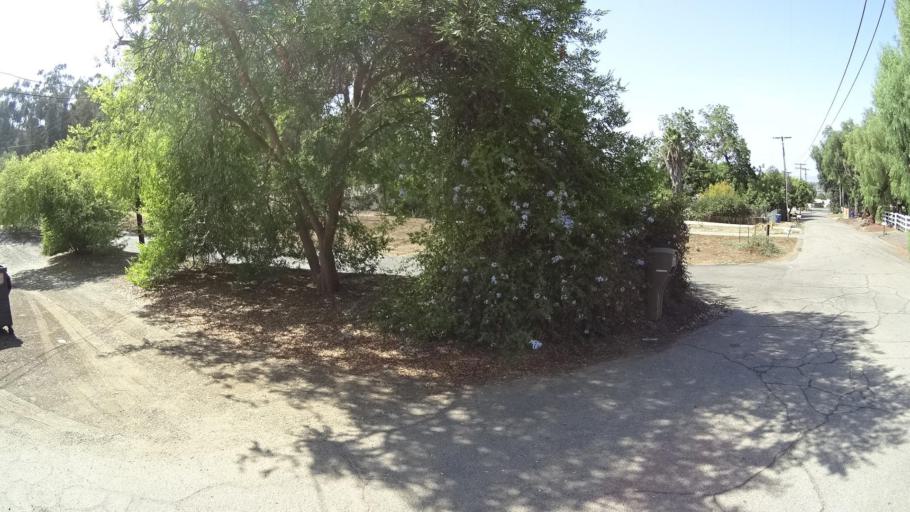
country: US
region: California
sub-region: San Diego County
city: Granite Hills
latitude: 32.7782
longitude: -116.9177
